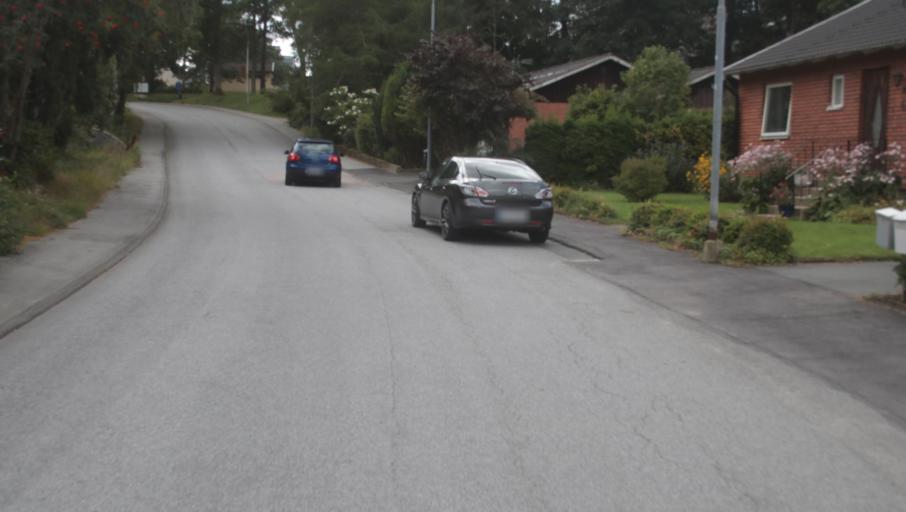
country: SE
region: Blekinge
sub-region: Karlshamns Kommun
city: Karlshamn
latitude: 56.1736
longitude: 14.8502
